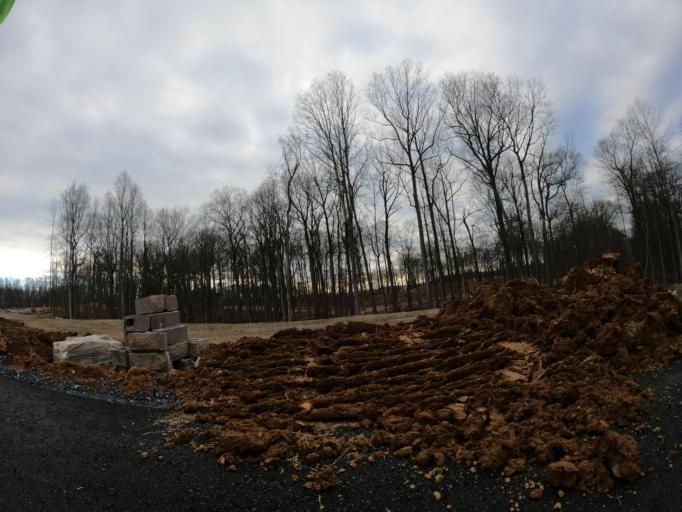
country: US
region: Maryland
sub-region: Howard County
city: Columbia
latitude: 39.2704
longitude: -76.8783
